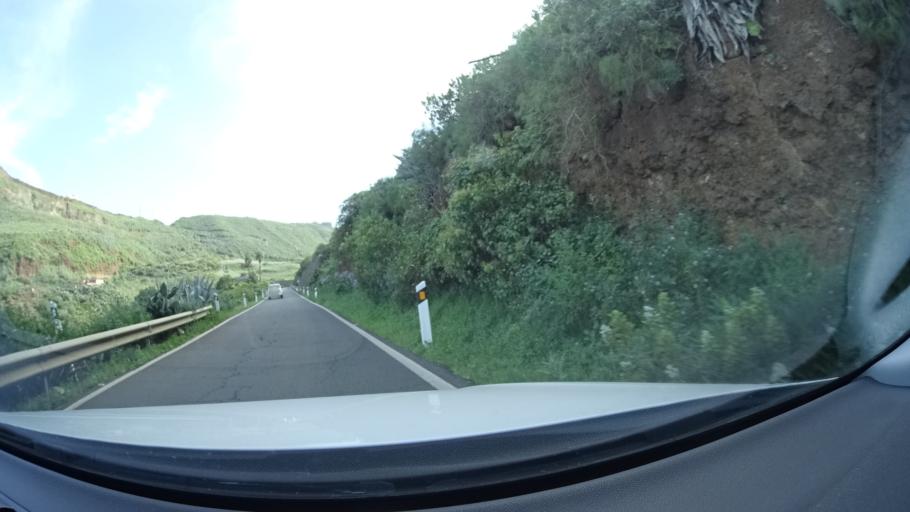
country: ES
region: Canary Islands
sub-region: Provincia de Las Palmas
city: Guia
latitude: 28.1102
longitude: -15.6417
